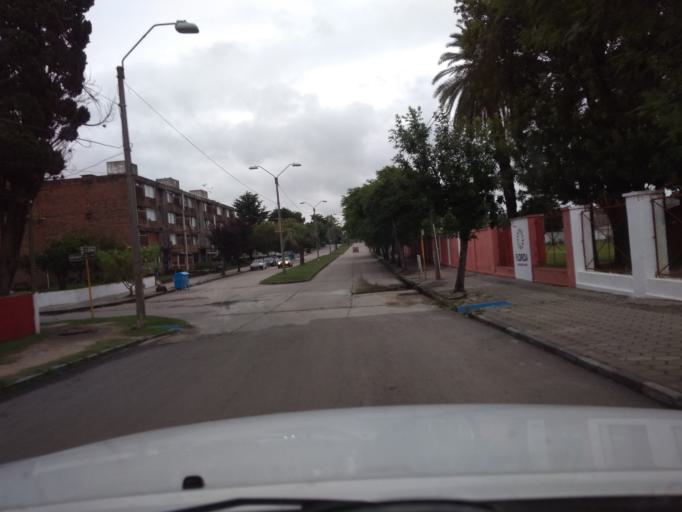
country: UY
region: Florida
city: Florida
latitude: -34.1041
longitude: -56.2087
